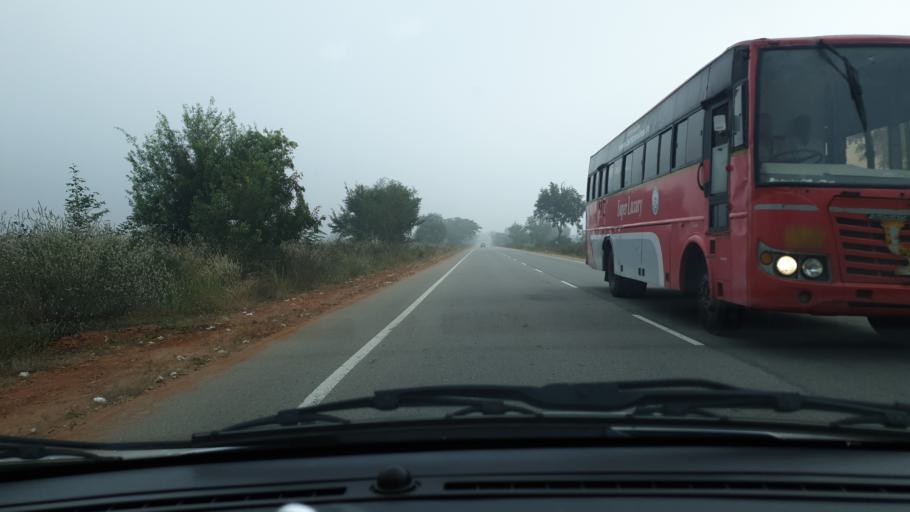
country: IN
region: Telangana
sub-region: Nalgonda
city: Devarkonda
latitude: 16.6370
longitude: 78.6232
